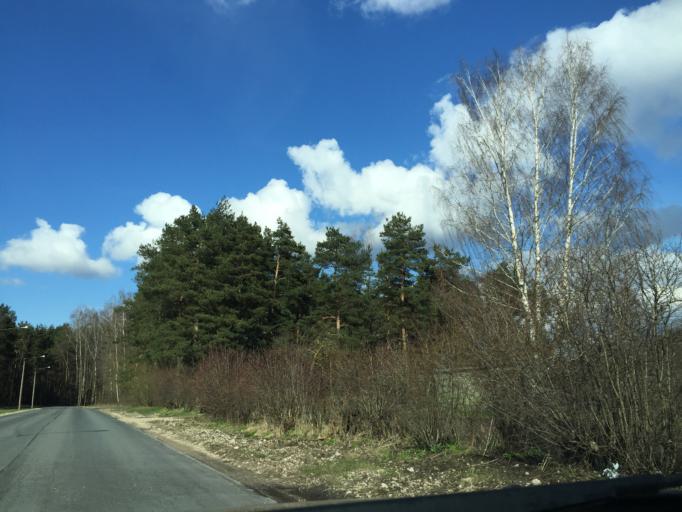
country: LV
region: Kekava
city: Kekava
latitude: 56.8224
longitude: 24.2114
